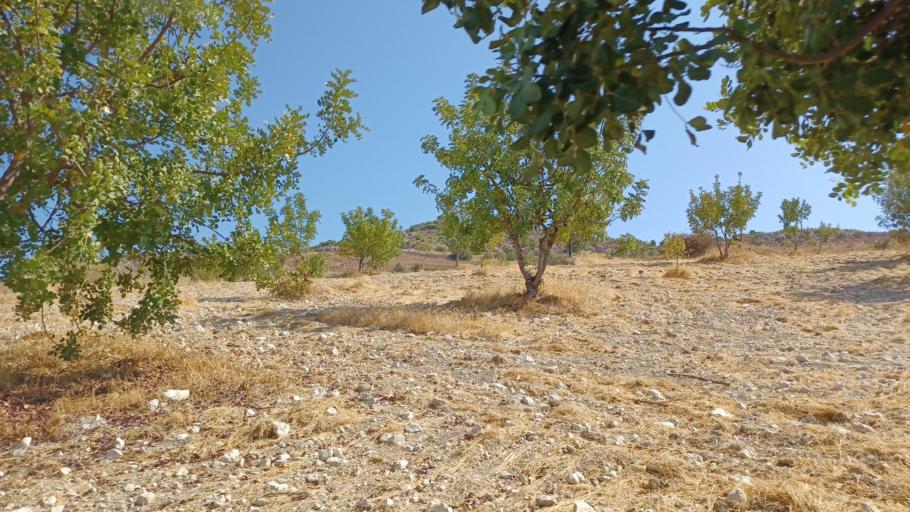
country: CY
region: Pafos
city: Polis
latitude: 34.9714
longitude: 32.4947
